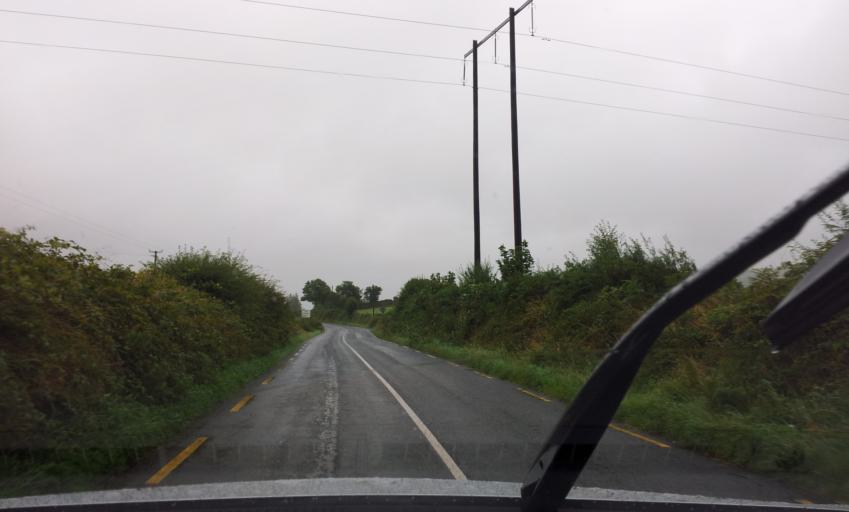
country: IE
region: Leinster
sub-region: Kilkenny
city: Thomastown
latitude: 52.4085
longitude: -7.0718
